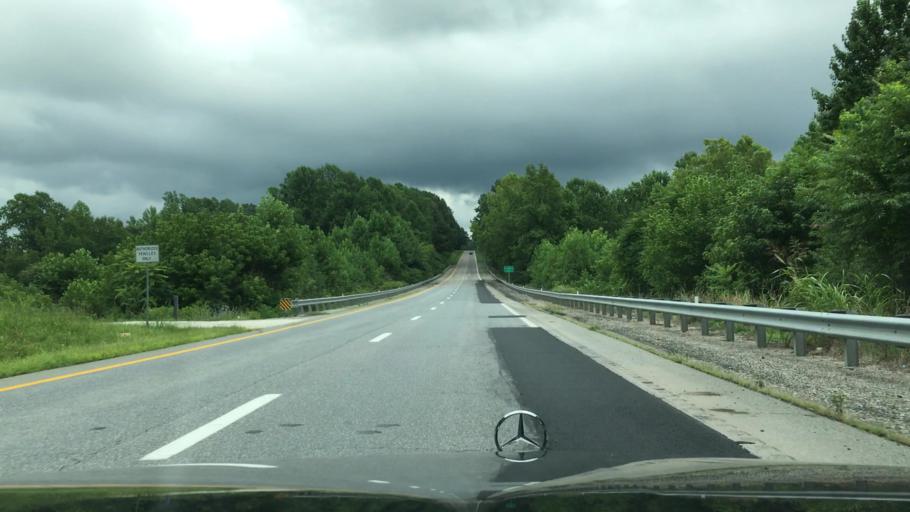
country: US
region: Virginia
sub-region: Appomattox County
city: Appomattox
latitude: 37.2710
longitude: -78.6722
